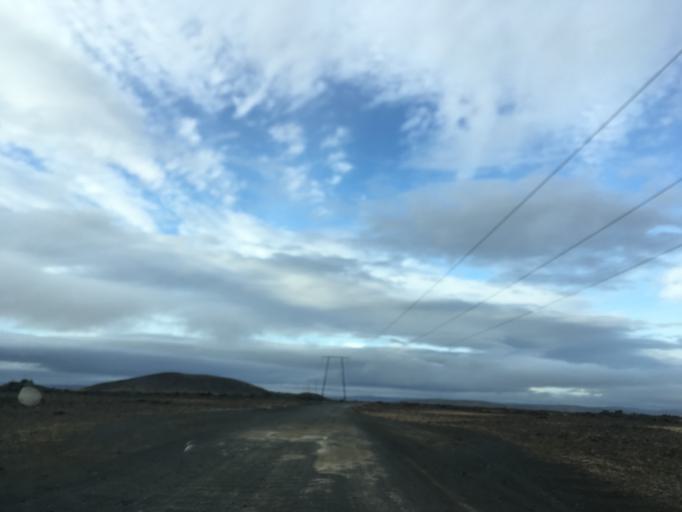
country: IS
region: South
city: Vestmannaeyjar
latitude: 64.1185
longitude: -19.1158
